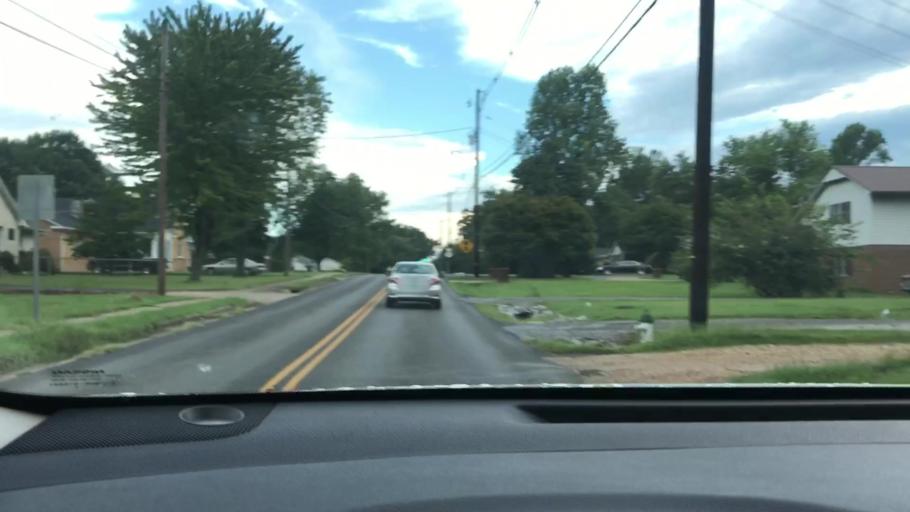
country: US
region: Kentucky
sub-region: Calloway County
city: Murray
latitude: 36.6049
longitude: -88.3245
